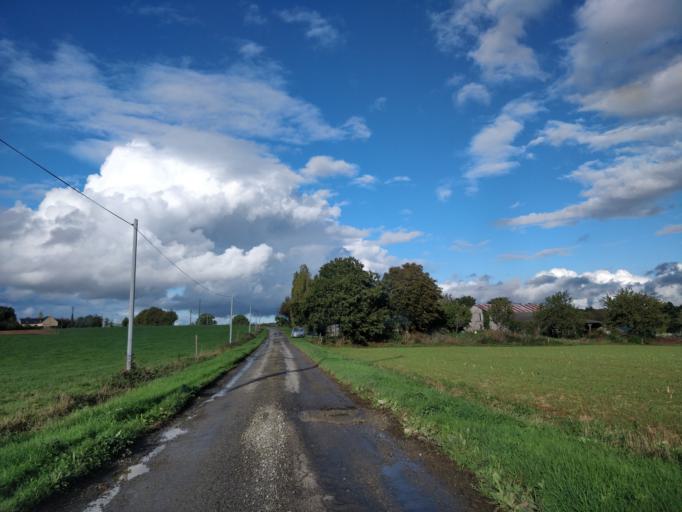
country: FR
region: Brittany
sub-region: Departement d'Ille-et-Vilaine
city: Chateaubourg
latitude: 48.1214
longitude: -1.4273
